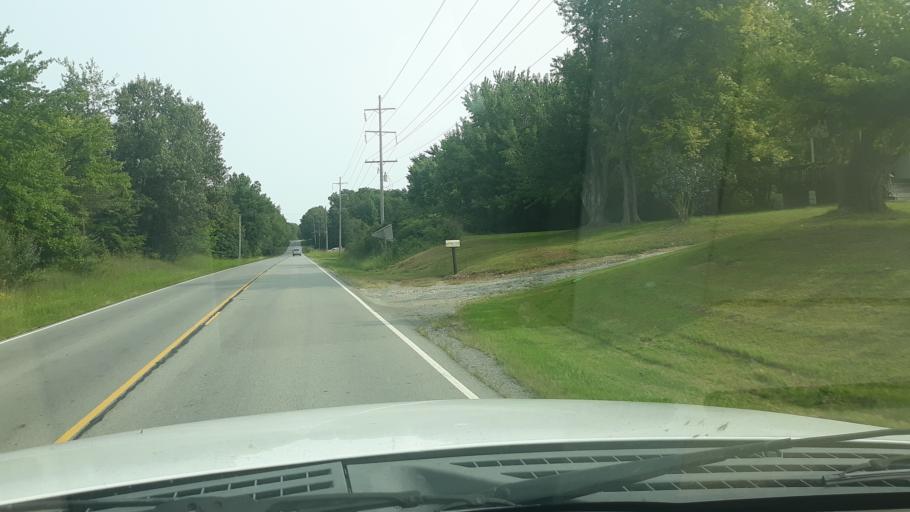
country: US
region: Illinois
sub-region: White County
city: Norris City
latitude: 37.9550
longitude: -88.3373
